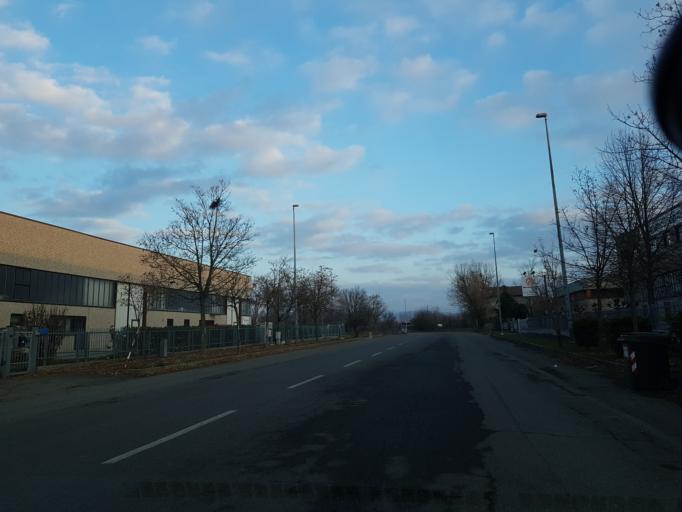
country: IT
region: Piedmont
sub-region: Provincia di Alessandria
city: Novi Ligure
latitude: 44.7551
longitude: 8.8121
